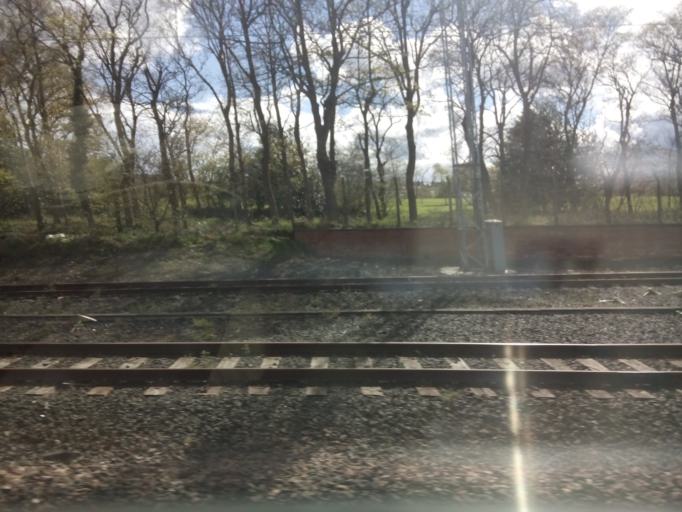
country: GB
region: Scotland
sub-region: West Lothian
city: Seafield
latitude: 55.9477
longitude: -3.1107
